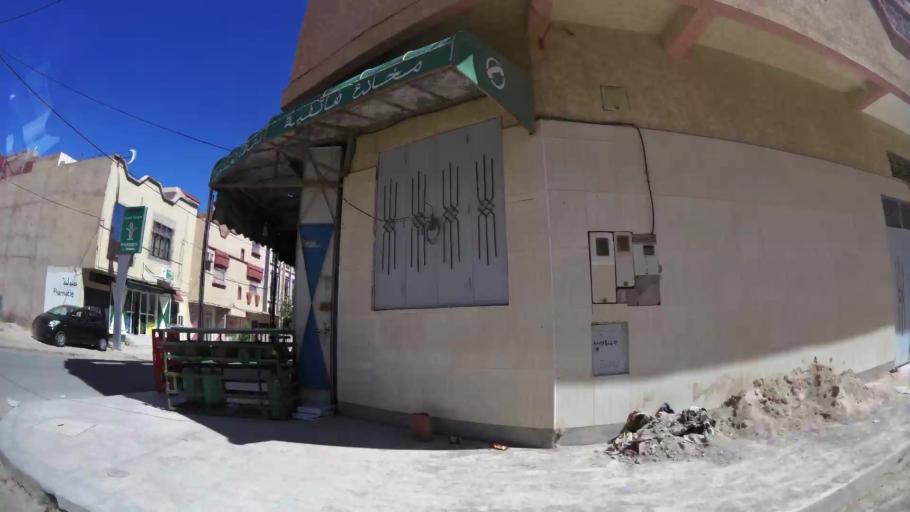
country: MA
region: Oriental
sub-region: Oujda-Angad
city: Oujda
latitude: 34.6625
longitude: -1.8882
